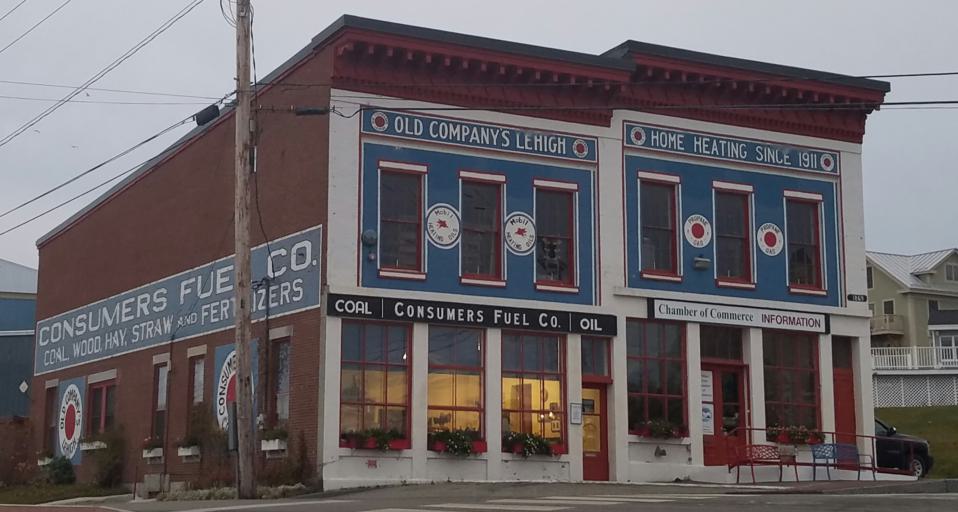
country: US
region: Maine
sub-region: Waldo County
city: Belfast
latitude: 44.4270
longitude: -69.0073
